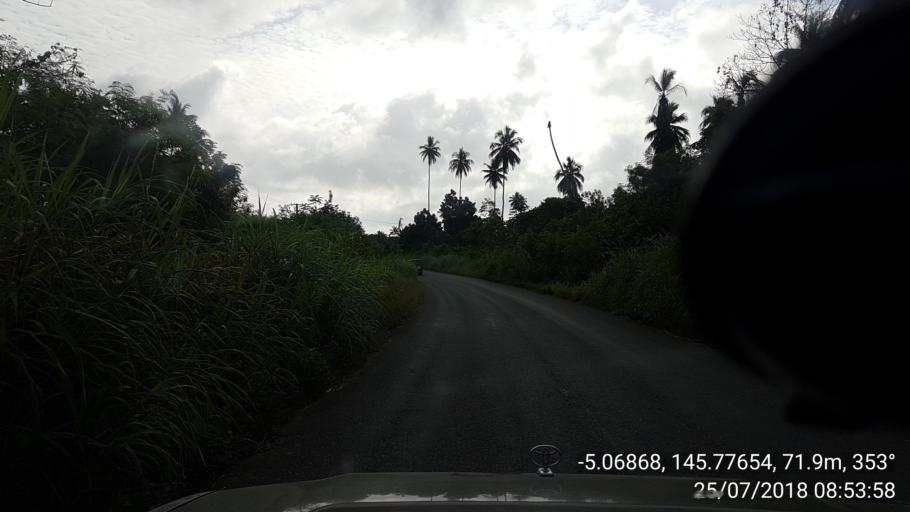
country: PG
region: Madang
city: Madang
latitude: -5.0686
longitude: 145.7767
